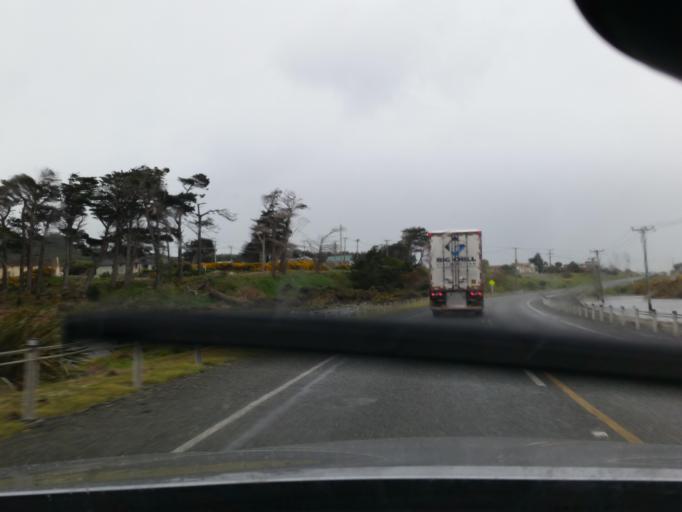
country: NZ
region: Southland
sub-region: Invercargill City
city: Bluff
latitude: -46.5873
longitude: 168.3050
